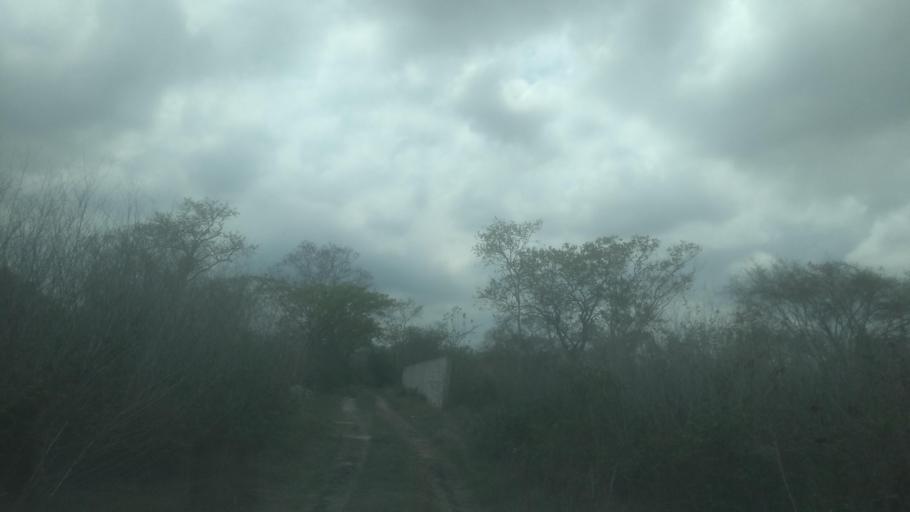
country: MX
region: Veracruz
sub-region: Emiliano Zapata
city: Plan del Rio
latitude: 19.3867
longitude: -96.6329
